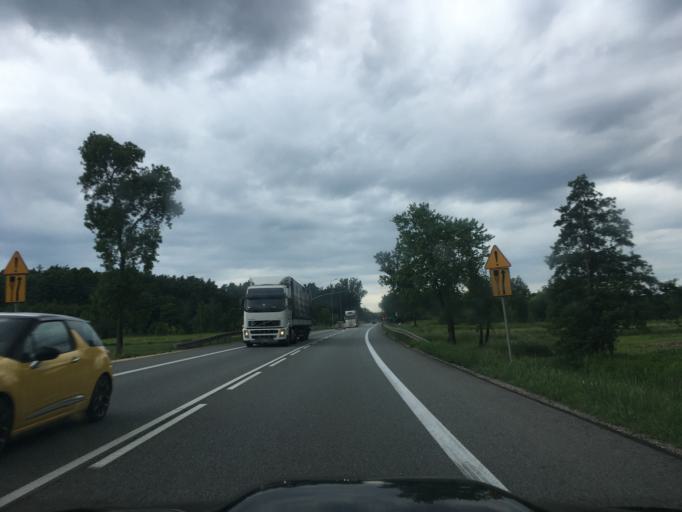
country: PL
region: Masovian Voivodeship
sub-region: Powiat otwocki
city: Celestynow
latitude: 52.0409
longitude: 21.3931
